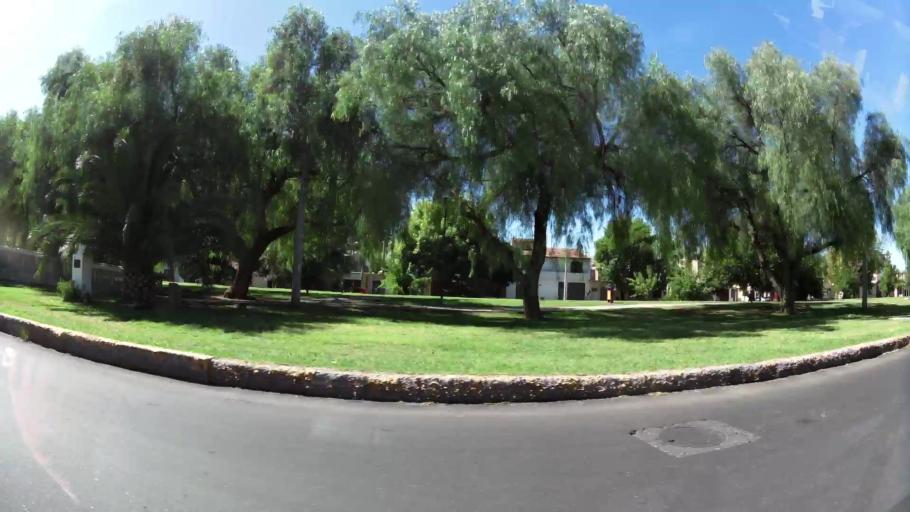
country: AR
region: Mendoza
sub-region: Departamento de Godoy Cruz
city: Godoy Cruz
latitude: -32.9428
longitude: -68.8506
